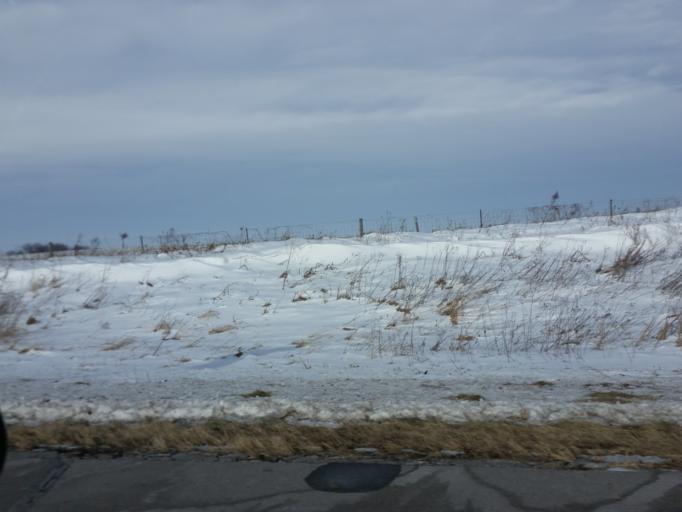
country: US
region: Iowa
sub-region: Buchanan County
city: Independence
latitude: 42.4617
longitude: -91.7426
